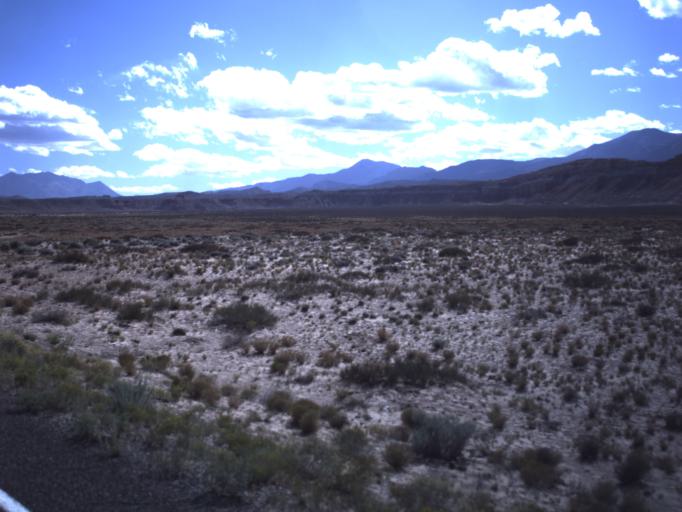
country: US
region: Utah
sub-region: Wayne County
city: Loa
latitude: 38.1786
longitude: -110.6256
